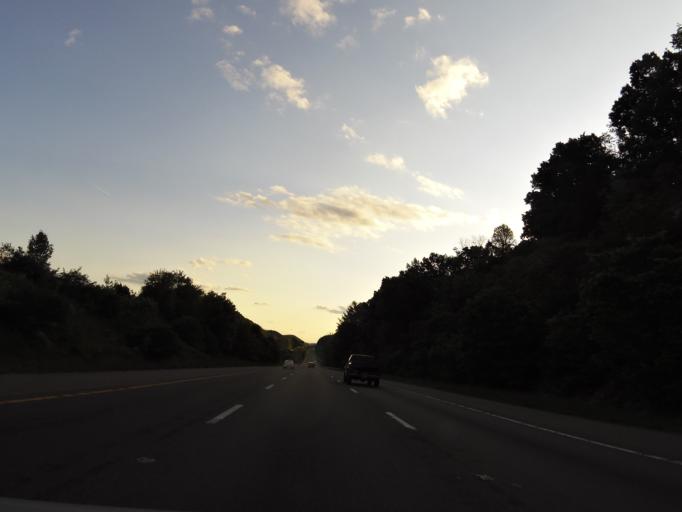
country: US
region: Virginia
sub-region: City of Bristol
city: Bristol
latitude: 36.6128
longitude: -82.2063
